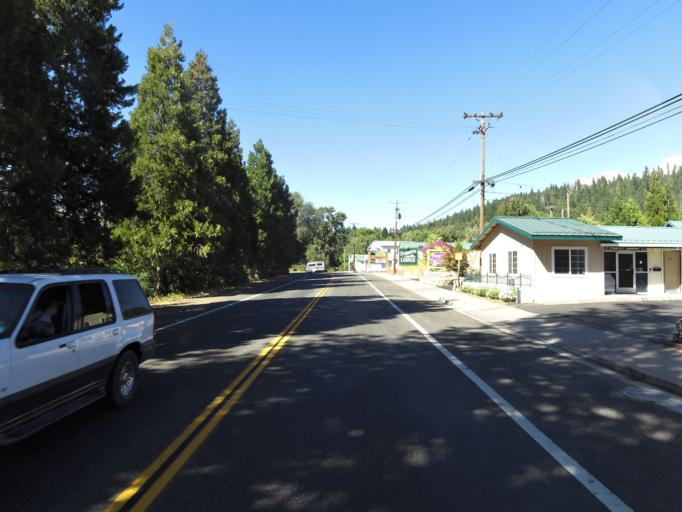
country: US
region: California
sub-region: Siskiyou County
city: Mount Shasta
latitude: 41.3007
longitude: -122.3062
